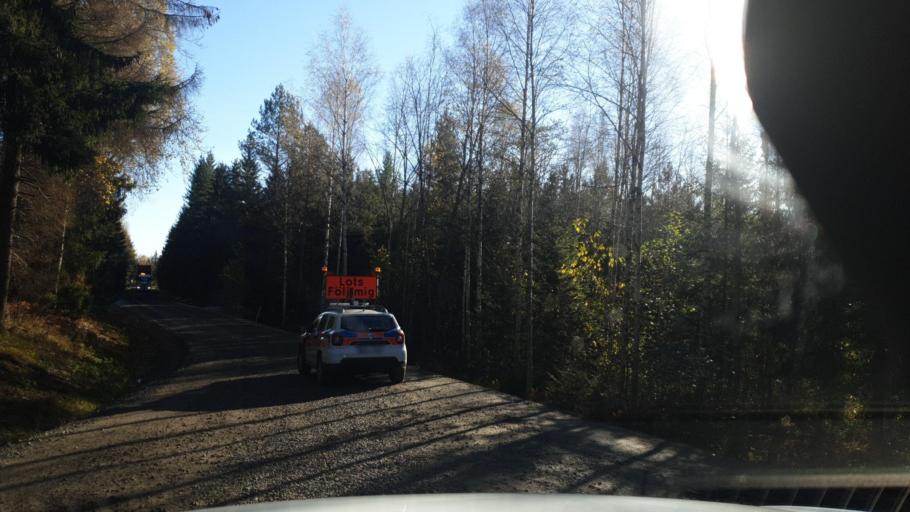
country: SE
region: Vaermland
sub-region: Karlstads Kommun
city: Valberg
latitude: 59.4154
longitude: 13.1533
